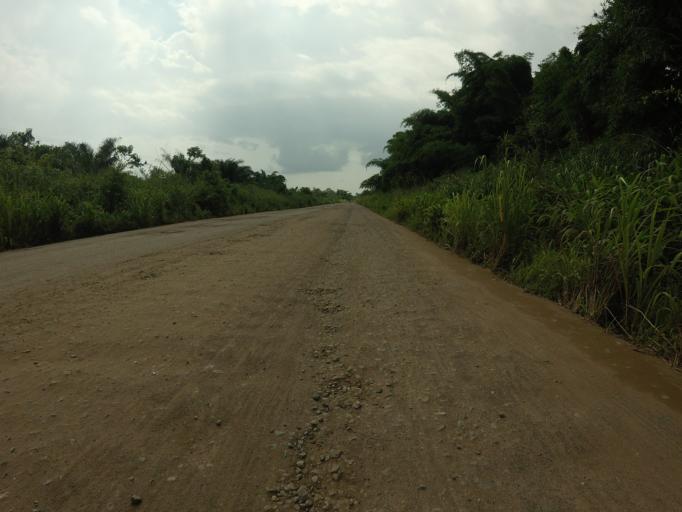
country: GH
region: Volta
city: Kpandu
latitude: 6.9728
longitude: 0.4520
